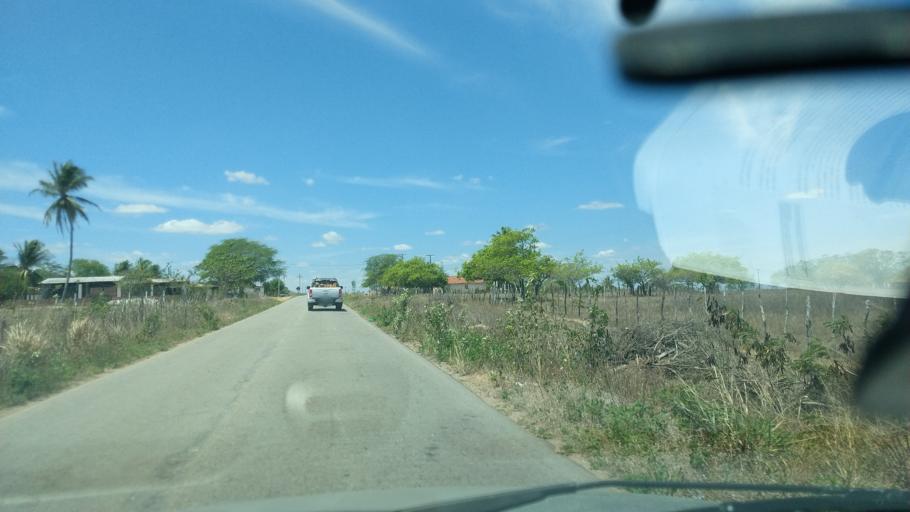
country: BR
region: Rio Grande do Norte
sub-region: Sao Paulo Do Potengi
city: Sao Paulo do Potengi
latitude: -5.9194
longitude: -35.5834
